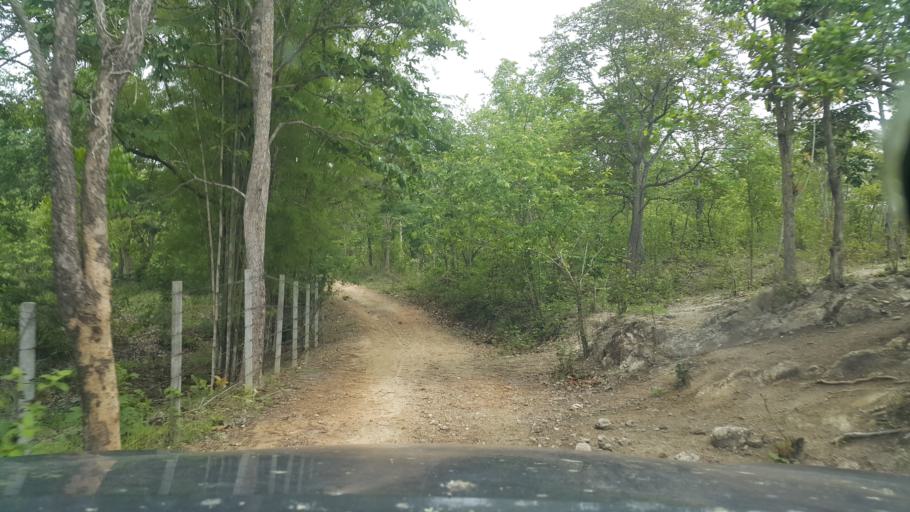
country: TH
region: Chiang Mai
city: Hang Dong
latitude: 18.6994
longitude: 98.8560
